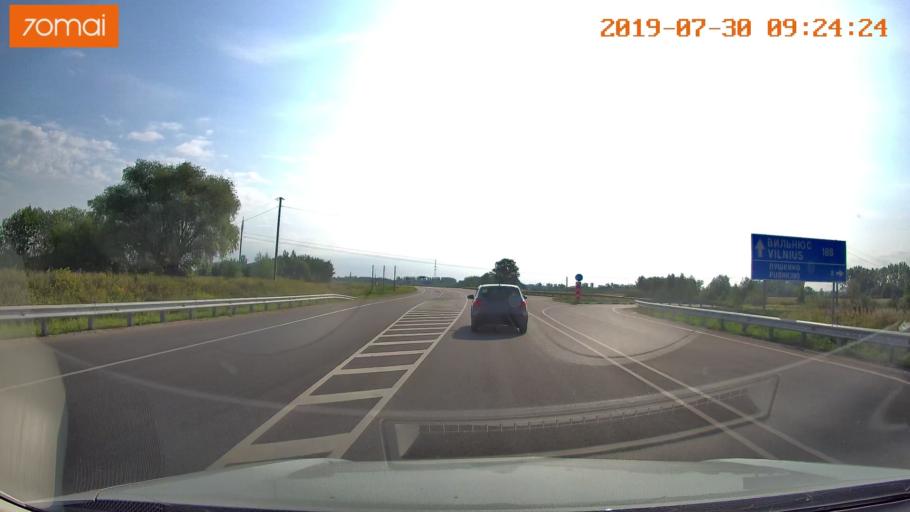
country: LT
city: Kybartai
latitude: 54.6332
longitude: 22.6933
